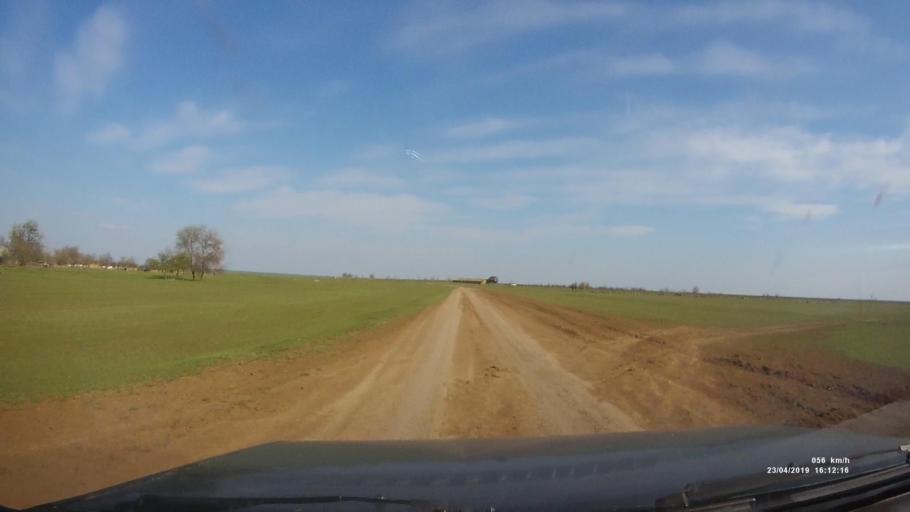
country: RU
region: Kalmykiya
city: Priyutnoye
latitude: 46.4673
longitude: 43.1246
